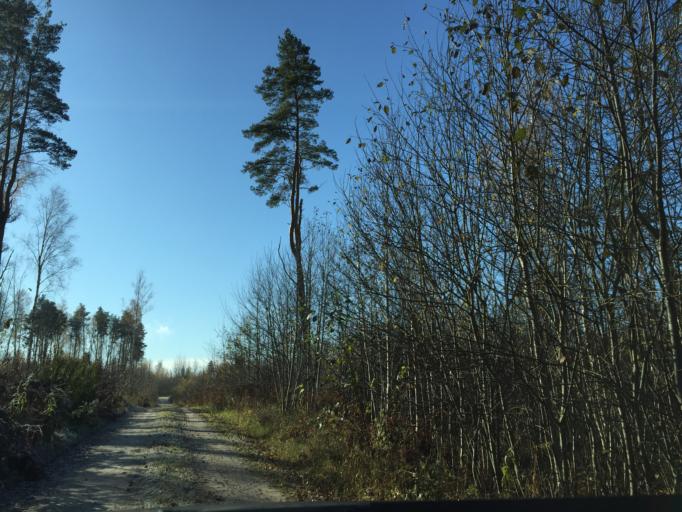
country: LV
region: Aizkraukles Rajons
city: Aizkraukle
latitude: 56.7167
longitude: 25.3003
